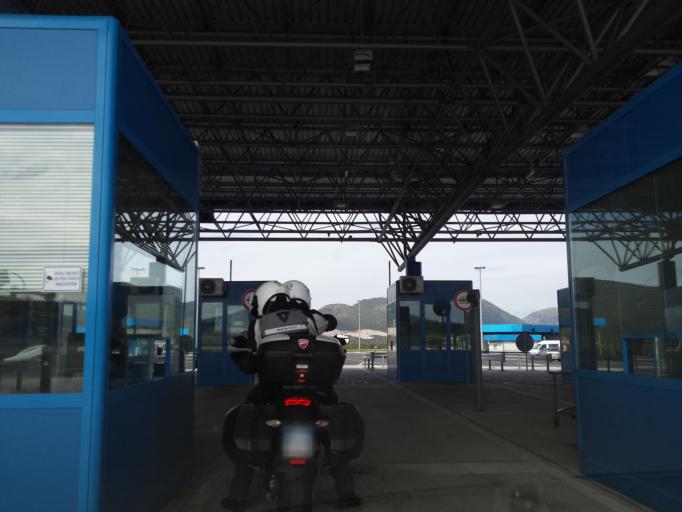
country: BA
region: Federation of Bosnia and Herzegovina
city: Ljubuski
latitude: 43.1235
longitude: 17.5606
